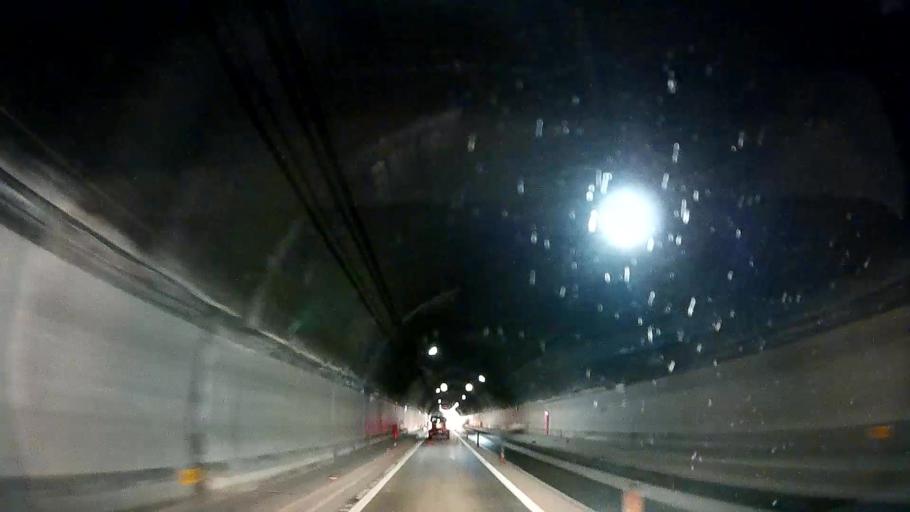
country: JP
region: Saitama
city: Chichibu
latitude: 35.9600
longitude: 139.1641
